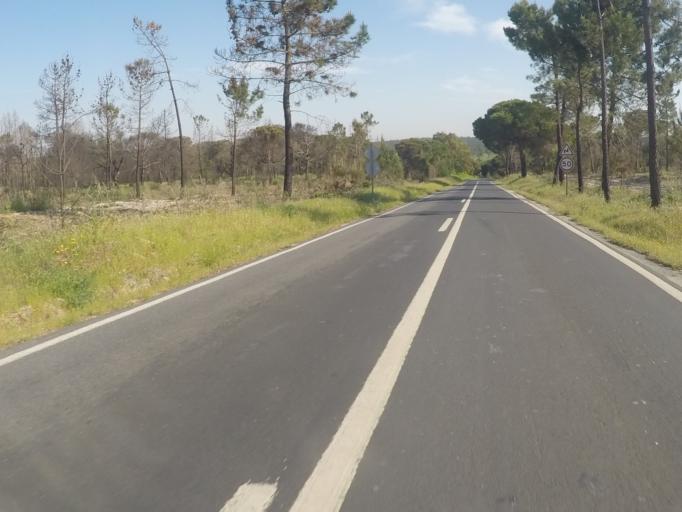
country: PT
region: Setubal
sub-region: Sesimbra
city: Sesimbra
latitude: 38.5200
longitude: -9.1435
